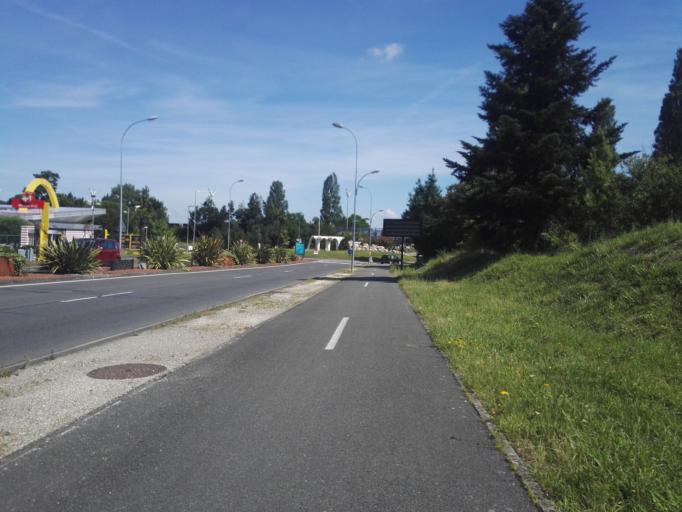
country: FR
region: Aquitaine
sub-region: Departement de la Gironde
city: Villenave-d'Ornon
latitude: 44.7773
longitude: -0.5702
